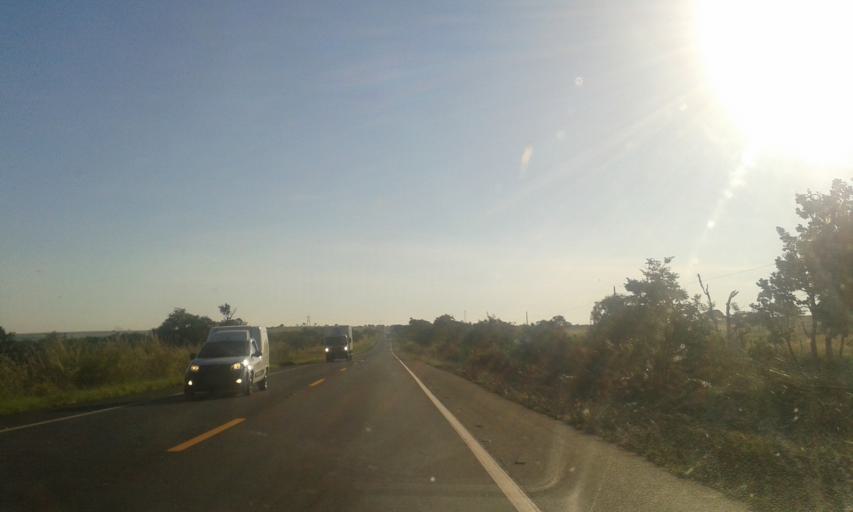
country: BR
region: Minas Gerais
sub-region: Monte Alegre De Minas
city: Monte Alegre de Minas
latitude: -18.8795
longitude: -49.1097
